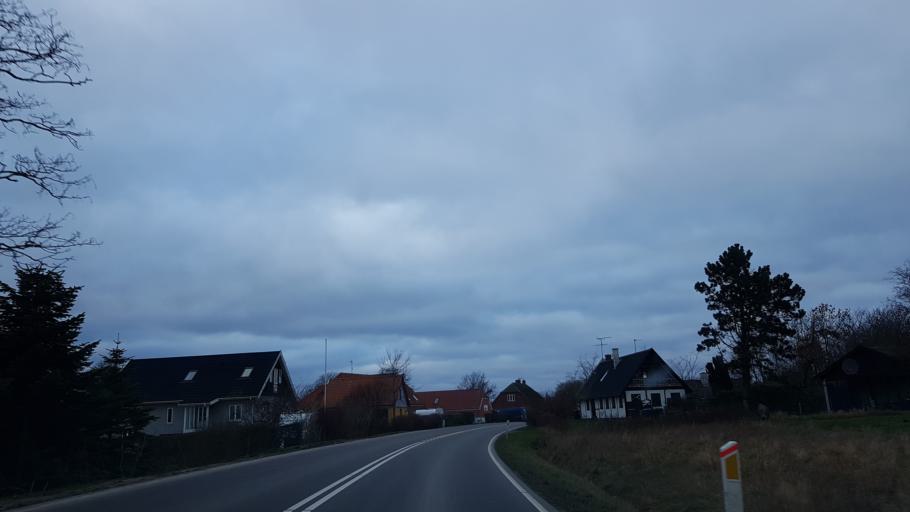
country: DK
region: Zealand
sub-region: Odsherred Kommune
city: Hojby
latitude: 55.9332
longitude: 11.5822
